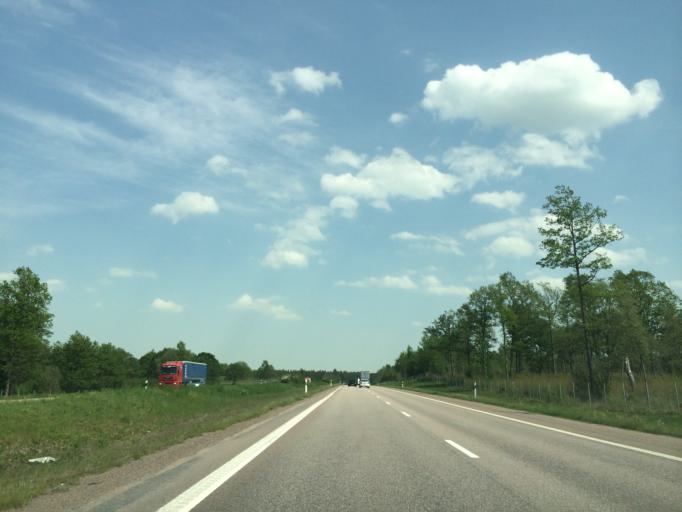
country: SE
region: OEstergoetland
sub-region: Boxholms Kommun
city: Boxholm
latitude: 58.3033
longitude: 14.9666
